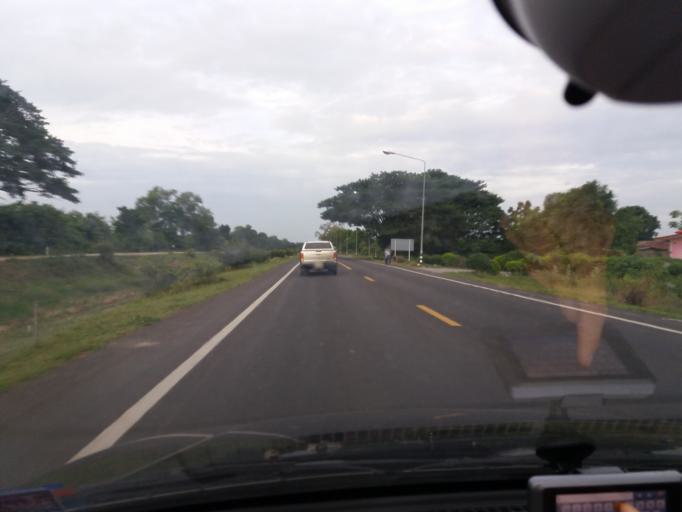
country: TH
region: Suphan Buri
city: Don Chedi
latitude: 14.5307
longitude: 99.9316
